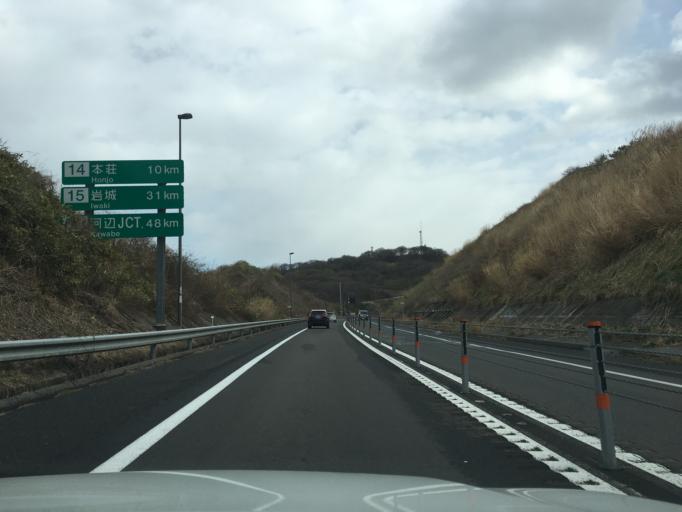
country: JP
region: Yamagata
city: Yuza
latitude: 39.3145
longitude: 139.9873
